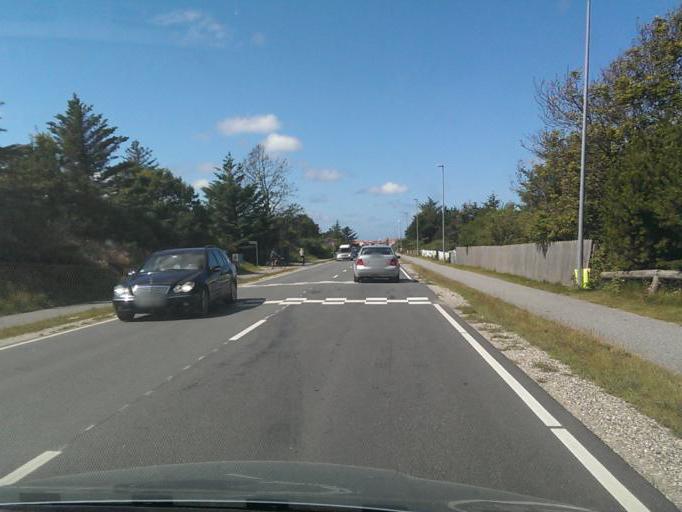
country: DK
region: North Denmark
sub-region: Jammerbugt Kommune
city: Pandrup
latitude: 57.2504
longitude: 9.5971
